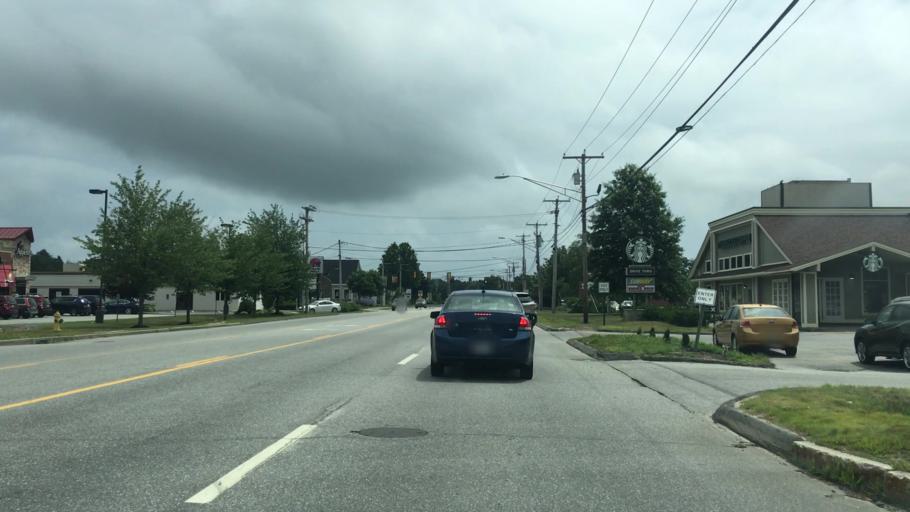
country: US
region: Maine
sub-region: Cumberland County
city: Brunswick
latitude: 43.9066
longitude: -69.9158
